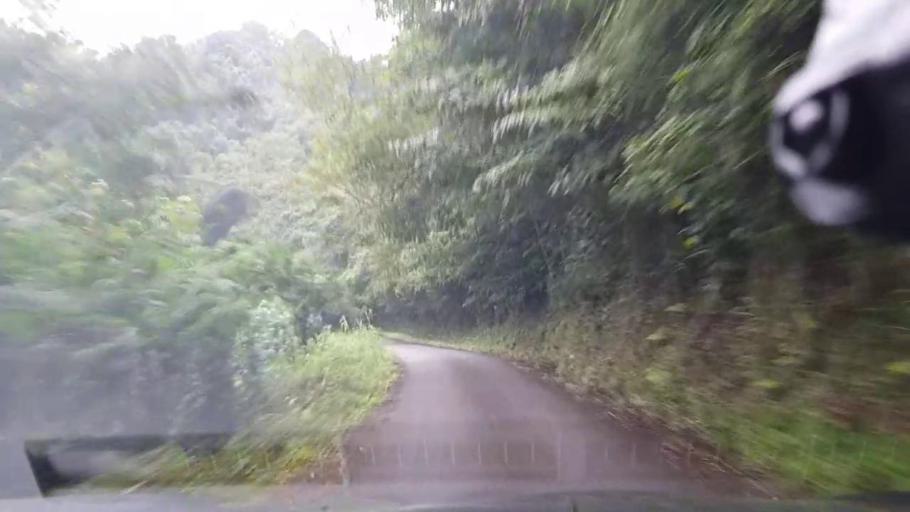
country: JM
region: Saint Andrew
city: Gordon Town
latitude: 18.1059
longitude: -76.7168
